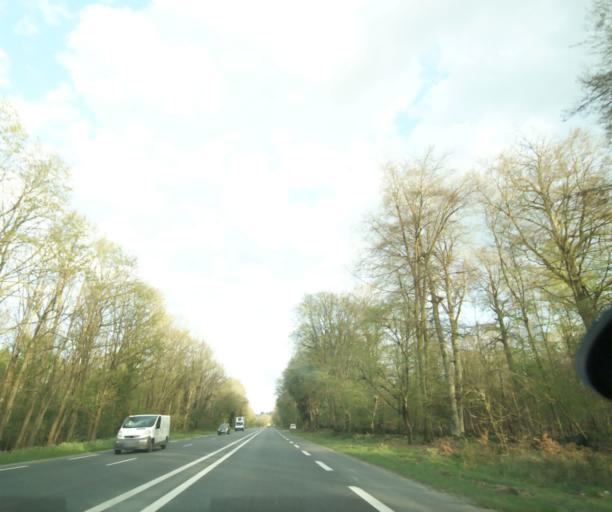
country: FR
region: Ile-de-France
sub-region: Departement de Seine-et-Marne
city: Barbizon
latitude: 48.4485
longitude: 2.6307
